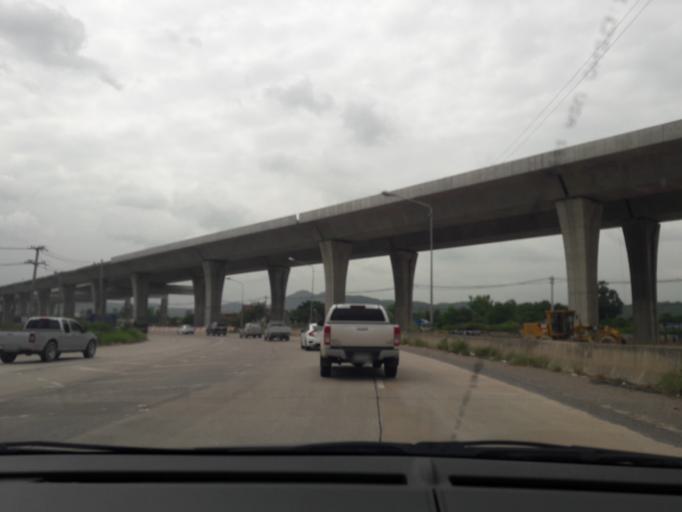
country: TH
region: Sara Buri
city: Saraburi
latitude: 14.4585
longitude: 100.9076
